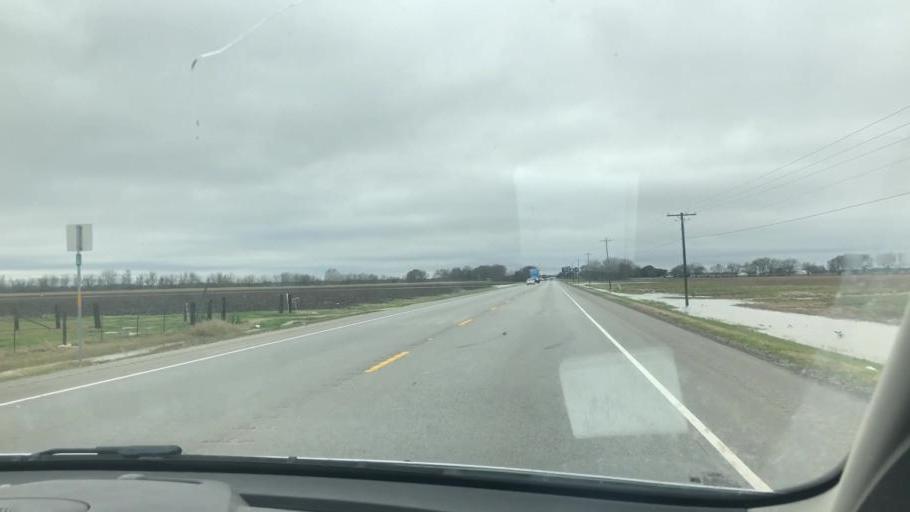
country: US
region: Texas
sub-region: Matagorda County
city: Bay City
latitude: 29.0503
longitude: -95.9712
